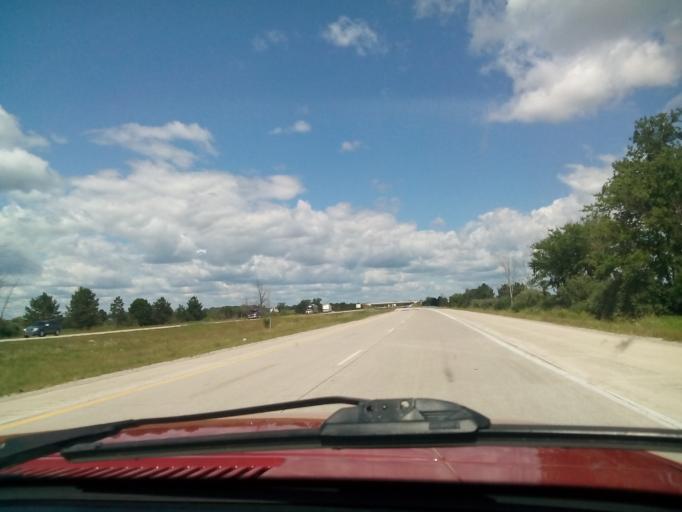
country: US
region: Michigan
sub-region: Bay County
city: Pinconning
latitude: 43.8605
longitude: -84.0204
